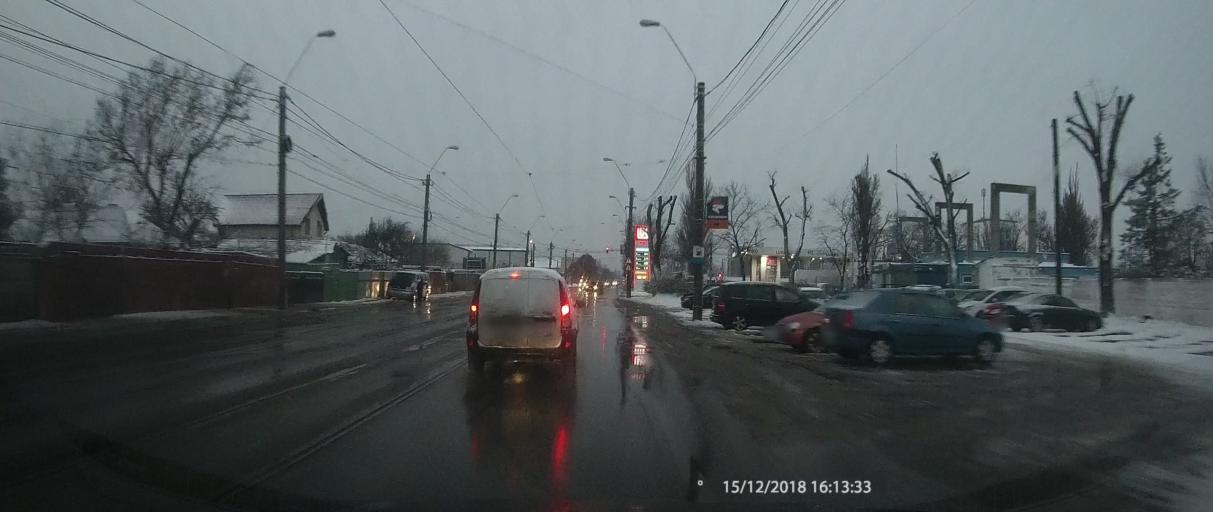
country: RO
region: Galati
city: Galati
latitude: 45.4626
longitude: 28.0337
